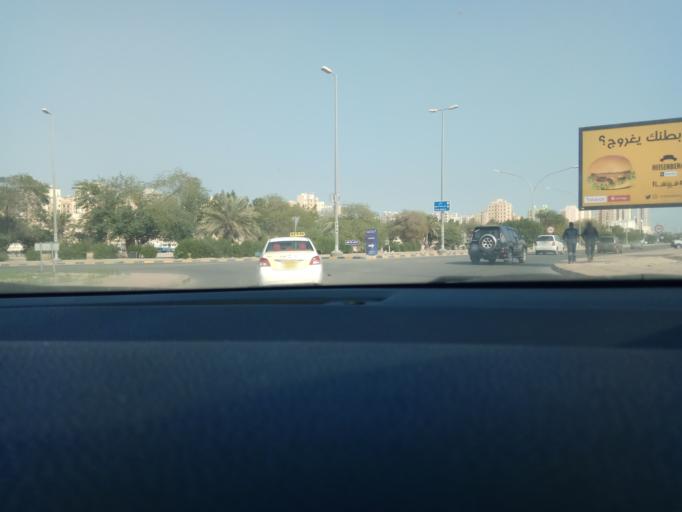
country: KW
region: Al Ahmadi
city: Al Fahahil
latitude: 29.0773
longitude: 48.1245
